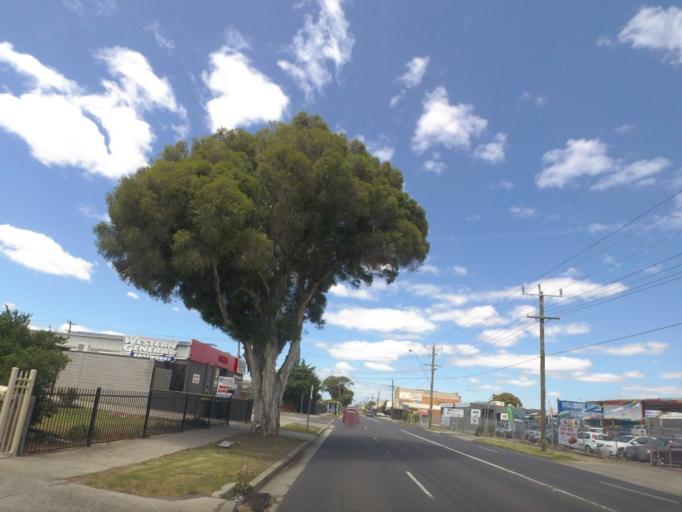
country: AU
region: Victoria
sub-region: Brimbank
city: Albion
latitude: -37.7675
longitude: 144.8306
